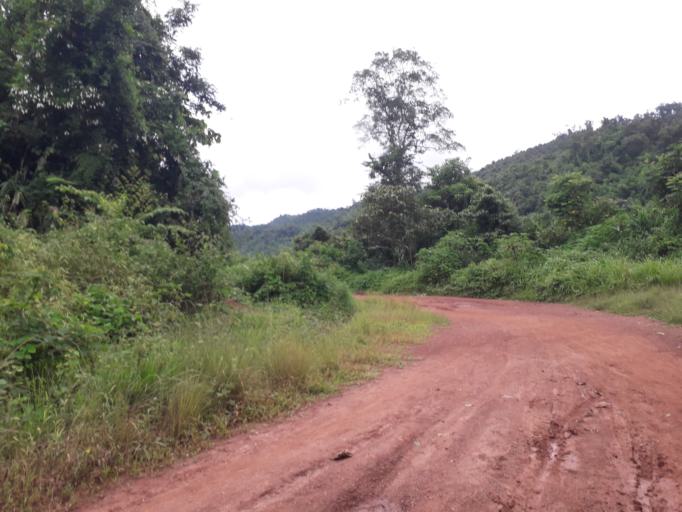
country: CN
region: Yunnan
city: Menglie
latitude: 22.2094
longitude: 101.6604
